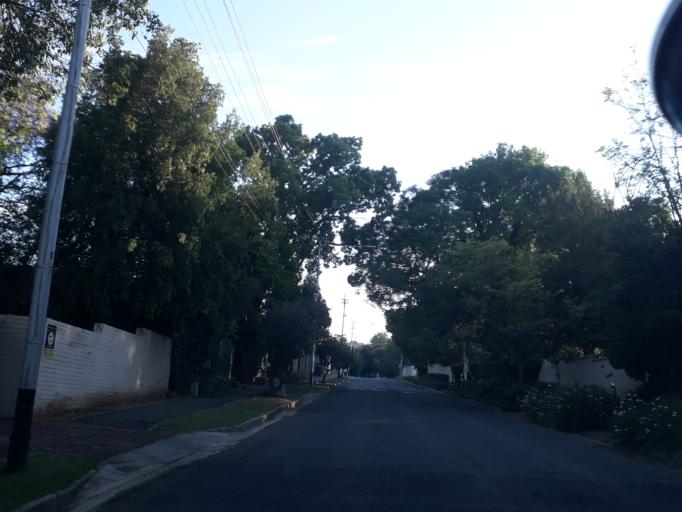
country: ZA
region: Gauteng
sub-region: City of Johannesburg Metropolitan Municipality
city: Johannesburg
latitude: -26.1135
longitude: 28.0277
